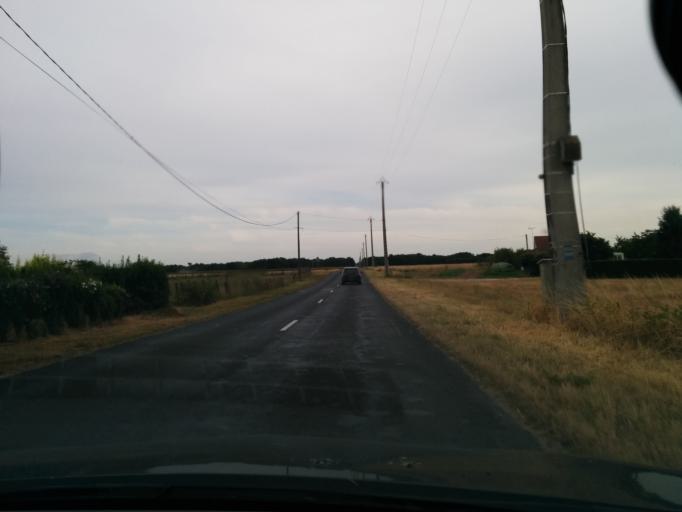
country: FR
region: Centre
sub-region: Departement du Loiret
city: Chateauneuf-sur-Loire
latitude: 47.8560
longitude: 2.2237
